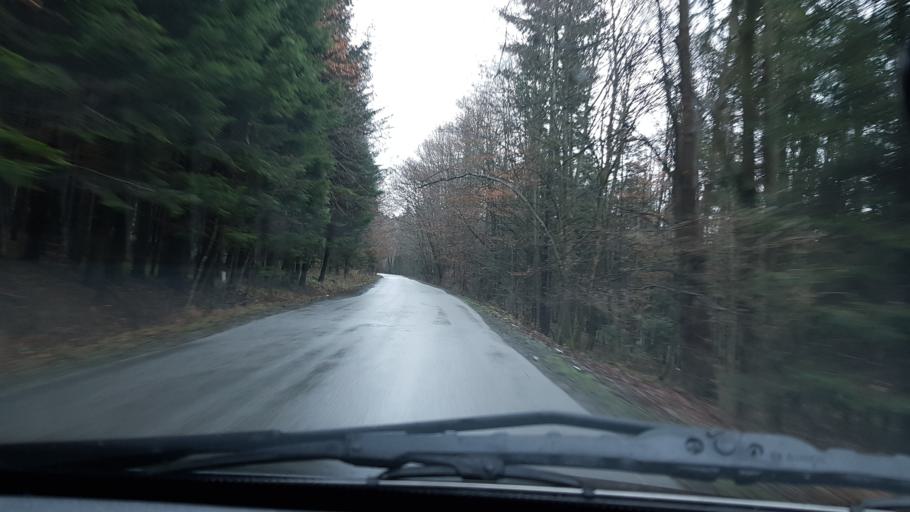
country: PL
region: Lesser Poland Voivodeship
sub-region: Powiat suski
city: Jordanow
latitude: 49.6329
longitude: 19.8411
